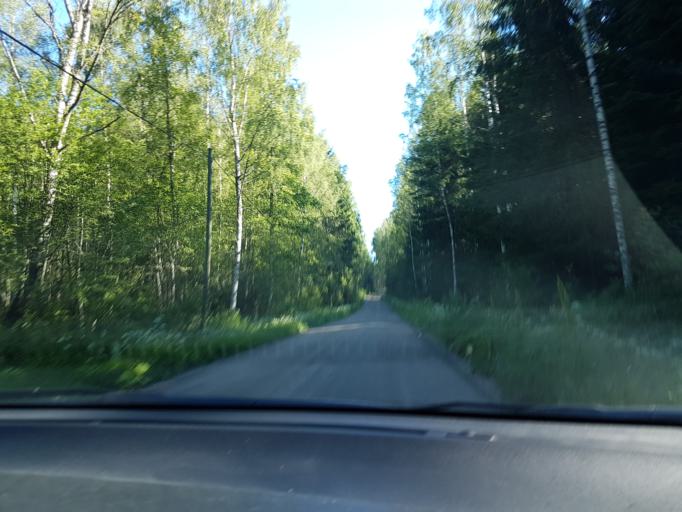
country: FI
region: Uusimaa
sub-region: Helsinki
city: Sibbo
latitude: 60.2677
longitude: 25.2289
